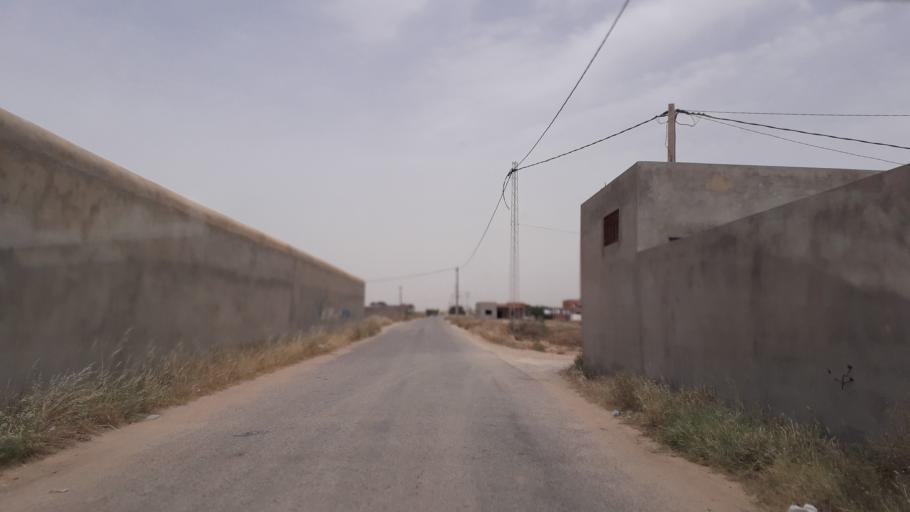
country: TN
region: Safaqis
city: Al Qarmadah
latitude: 34.8473
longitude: 10.7546
